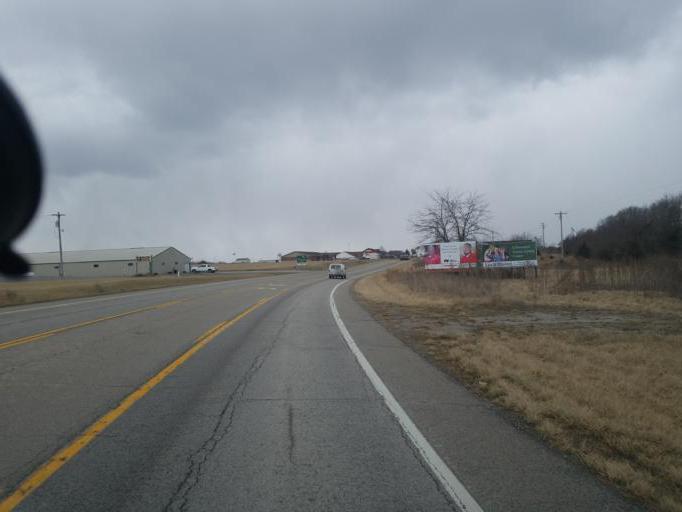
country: US
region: Missouri
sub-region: Macon County
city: Macon
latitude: 39.7636
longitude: -92.4677
